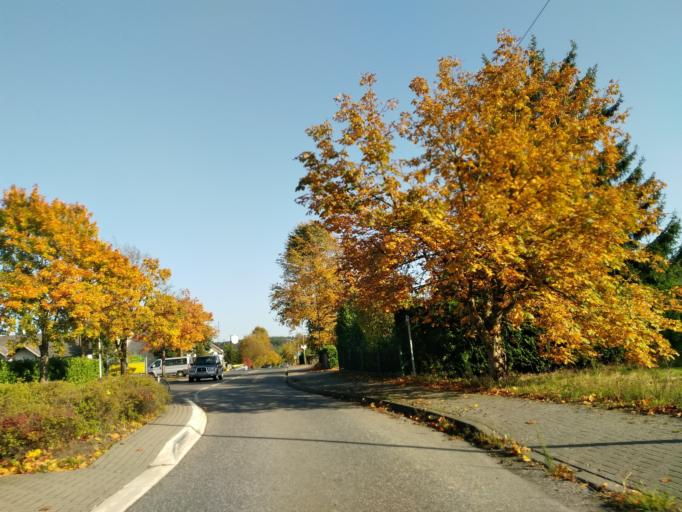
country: DE
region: Rheinland-Pfalz
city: Kircheib
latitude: 50.7094
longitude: 7.4552
